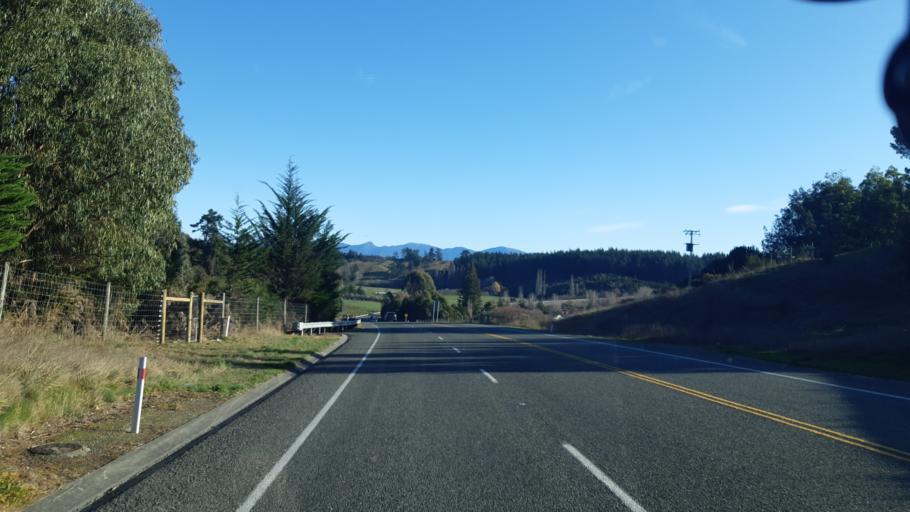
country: NZ
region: Tasman
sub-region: Tasman District
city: Mapua
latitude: -41.2836
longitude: 173.0763
